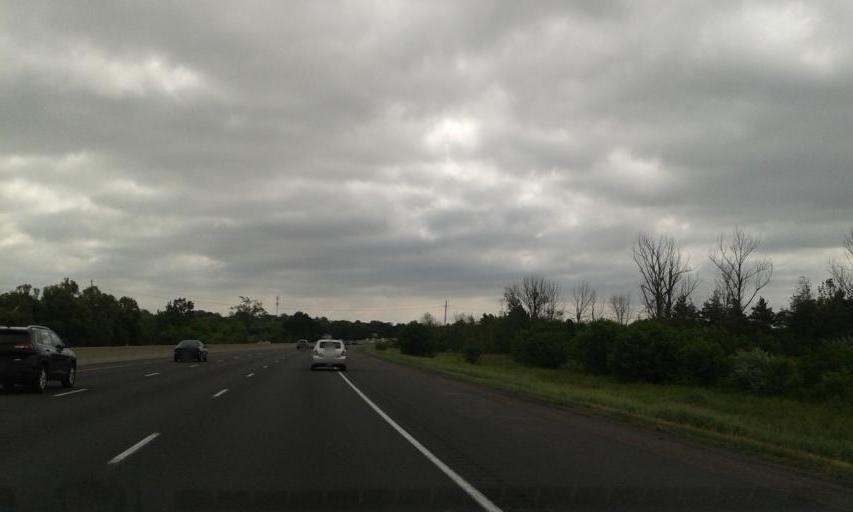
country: CA
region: Ontario
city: Oshawa
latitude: 43.8862
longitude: -78.8185
